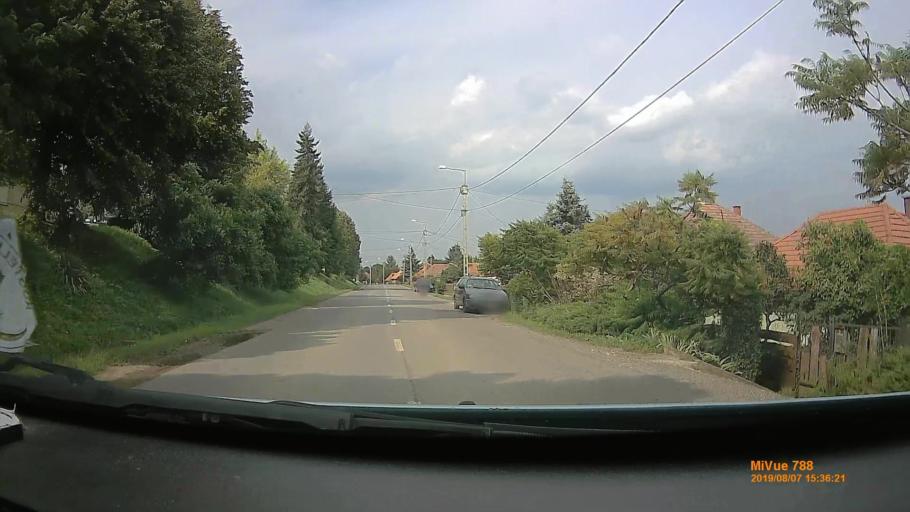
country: HU
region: Borsod-Abauj-Zemplen
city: Encs
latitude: 48.4114
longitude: 21.1734
